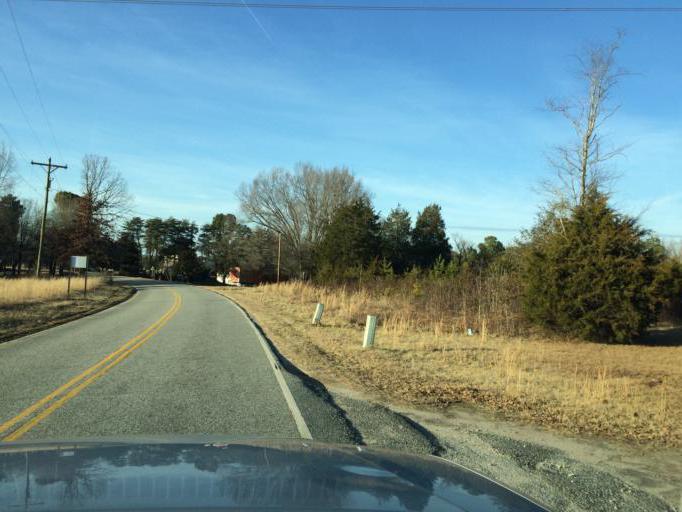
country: US
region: South Carolina
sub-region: Spartanburg County
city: Inman
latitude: 35.1412
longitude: -82.1007
